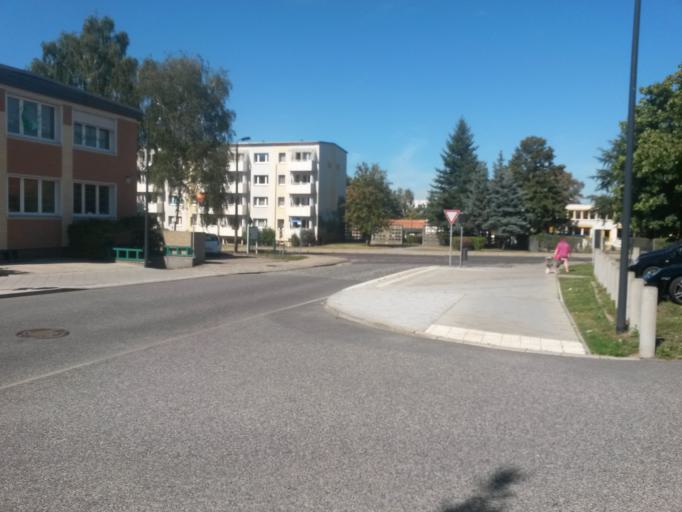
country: DE
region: Brandenburg
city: Prenzlau
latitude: 53.3166
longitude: 13.8585
